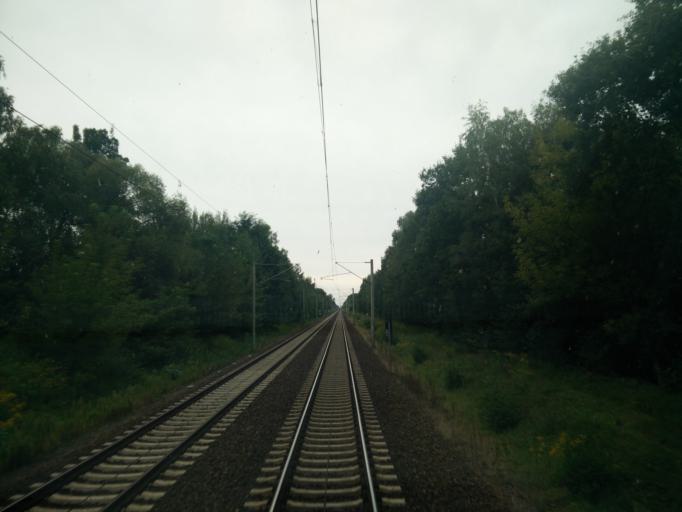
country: DE
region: Brandenburg
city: Dallgow-Doeberitz
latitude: 52.5672
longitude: 13.0609
